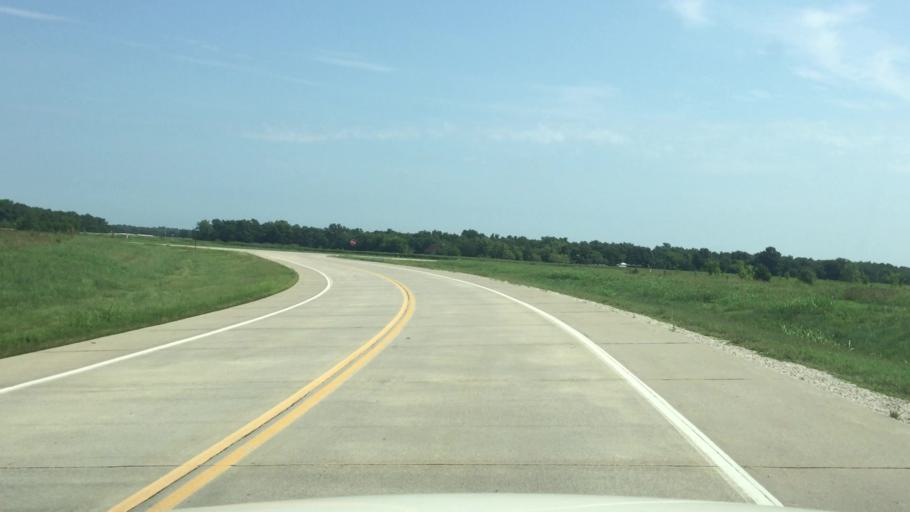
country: US
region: Kansas
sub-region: Montgomery County
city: Coffeyville
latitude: 37.1064
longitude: -95.5844
